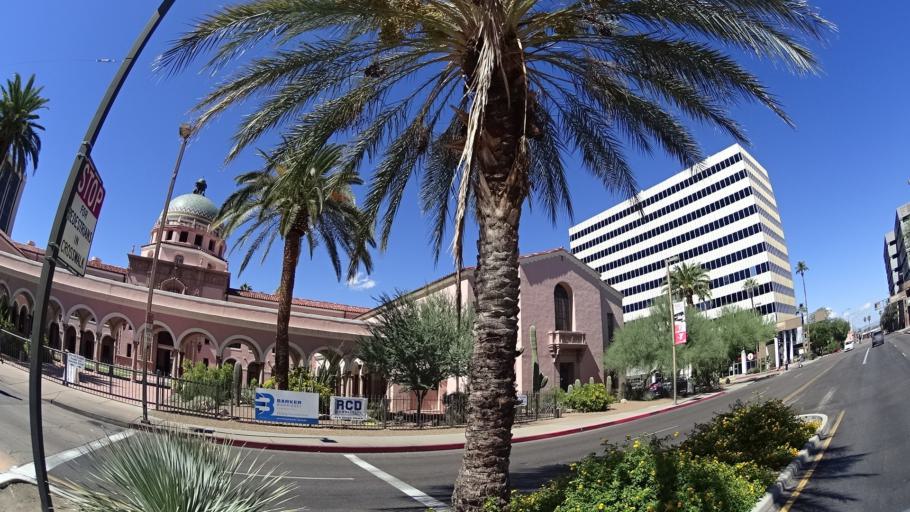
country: US
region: Arizona
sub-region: Pima County
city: South Tucson
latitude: 32.2232
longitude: -110.9727
